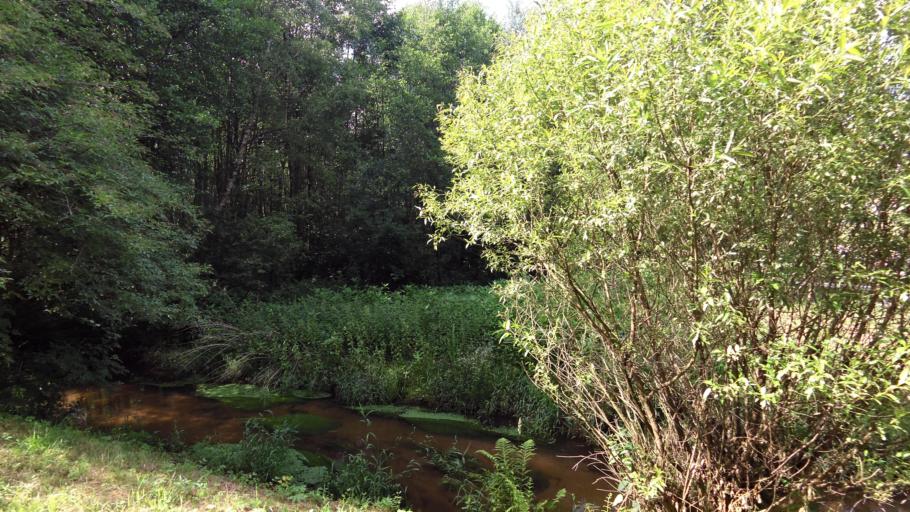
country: FR
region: Lorraine
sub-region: Departement de la Moselle
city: Abreschviller
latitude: 48.6321
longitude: 7.0987
